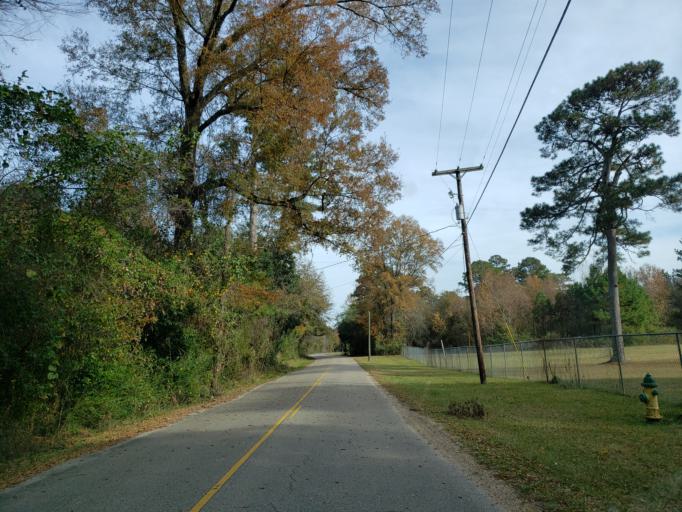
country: US
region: Mississippi
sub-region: Forrest County
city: Glendale
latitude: 31.3538
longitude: -89.3320
